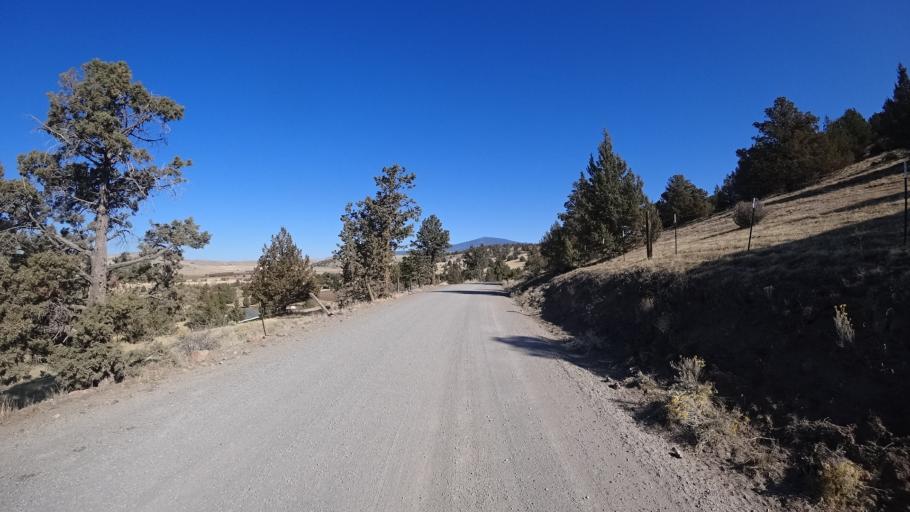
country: US
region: California
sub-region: Siskiyou County
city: Montague
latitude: 41.7143
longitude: -122.3753
